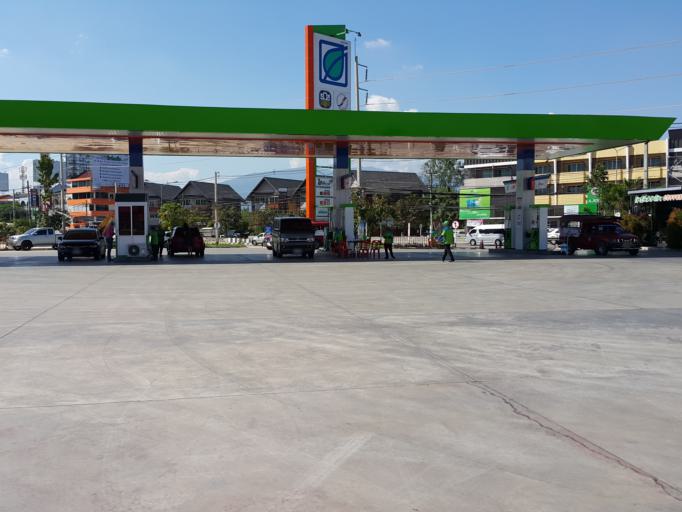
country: TH
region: Chiang Mai
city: Chiang Mai
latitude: 18.7616
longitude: 99.0230
